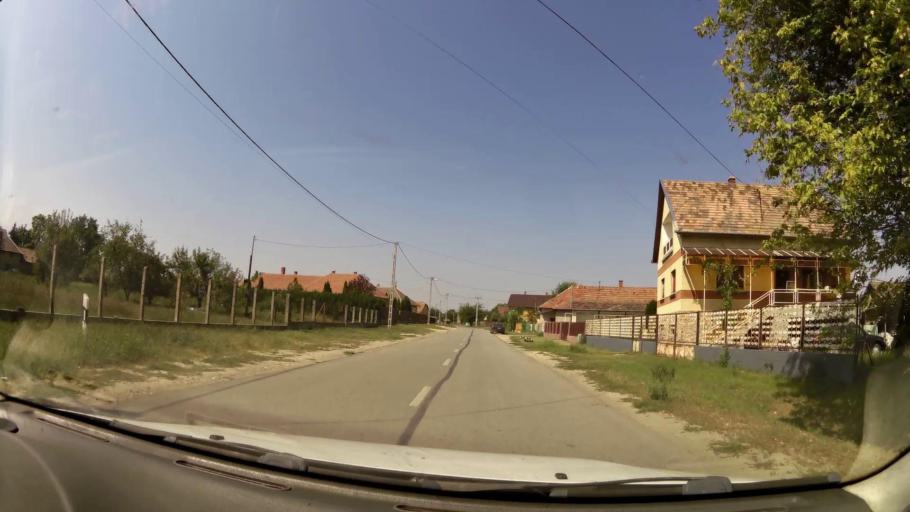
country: HU
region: Pest
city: Tapioszentmarton
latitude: 47.3431
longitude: 19.7764
